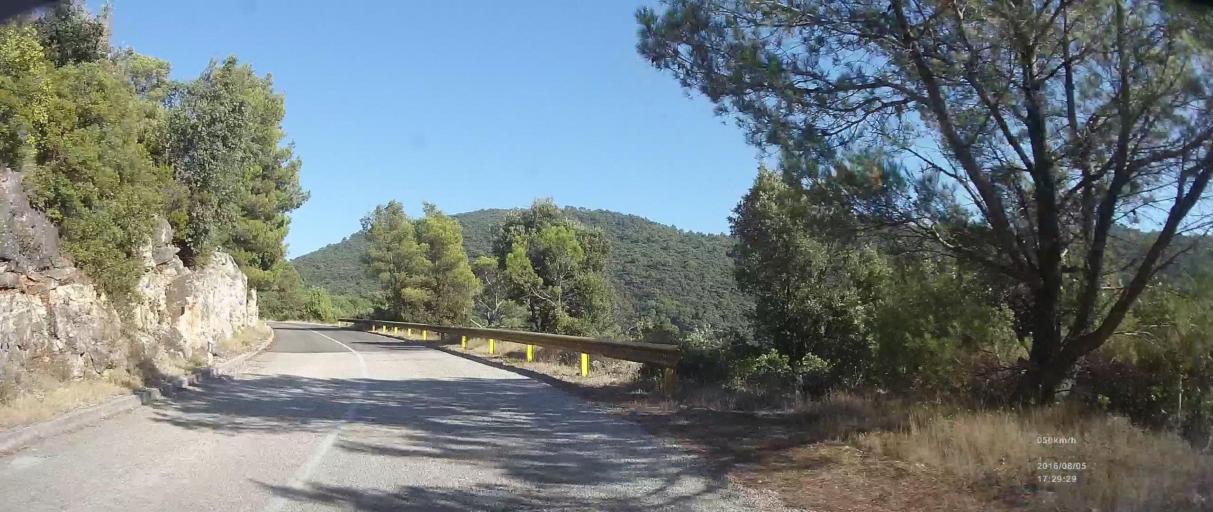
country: HR
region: Dubrovacko-Neretvanska
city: Blato
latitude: 42.7779
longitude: 17.4083
